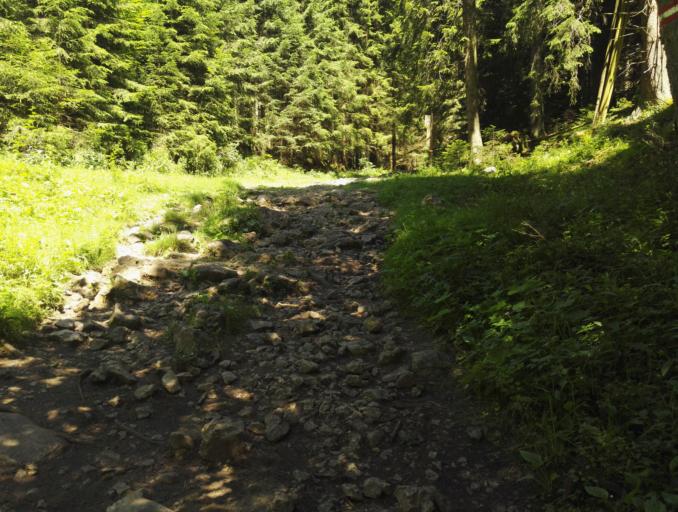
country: AT
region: Styria
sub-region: Politischer Bezirk Graz-Umgebung
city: Rothelstein
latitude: 47.3482
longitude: 15.4059
